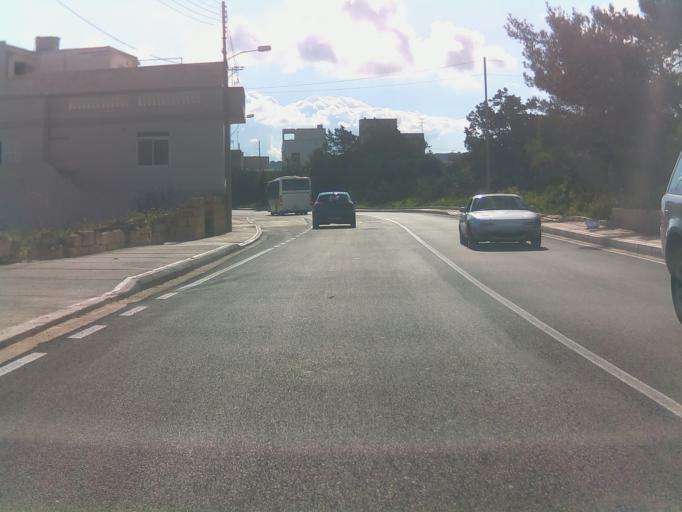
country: MT
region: L-Imgarr
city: Imgarr
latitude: 35.9283
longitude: 14.3676
